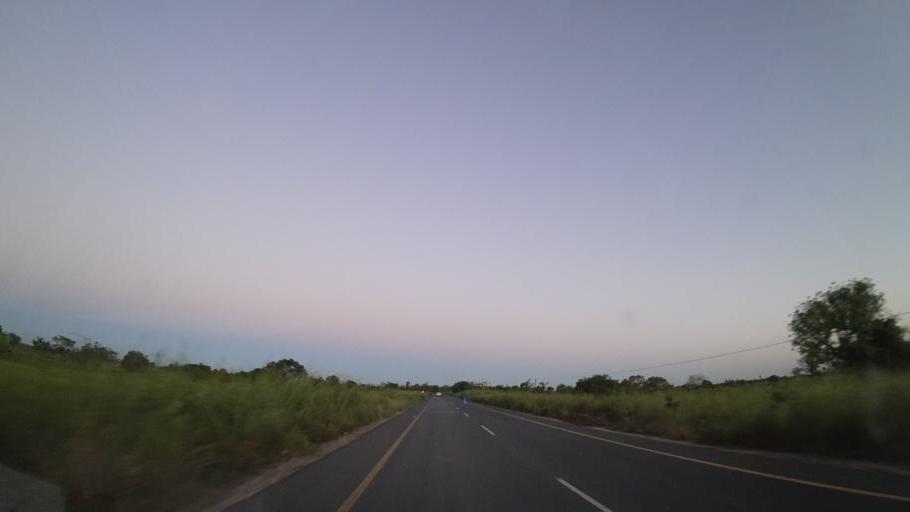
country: MZ
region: Sofala
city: Dondo
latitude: -19.5523
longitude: 34.6499
